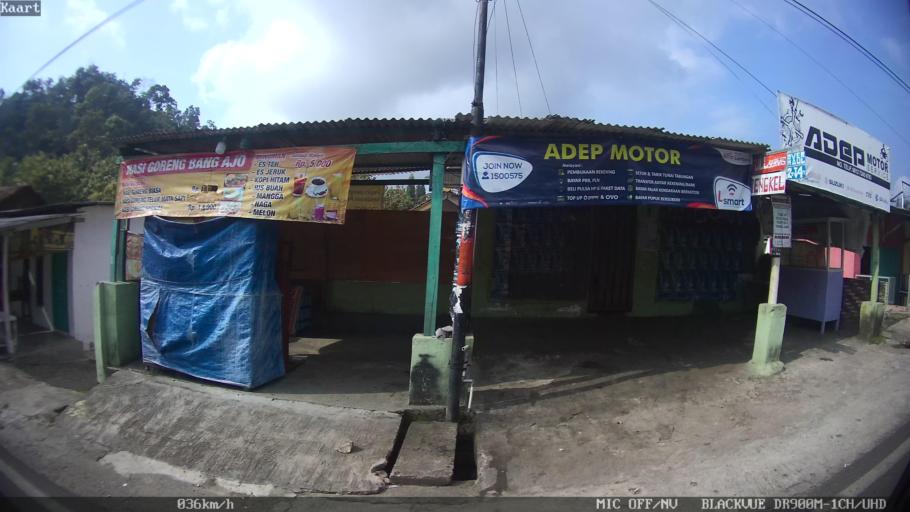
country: ID
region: Lampung
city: Kedaton
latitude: -5.3973
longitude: 105.2396
